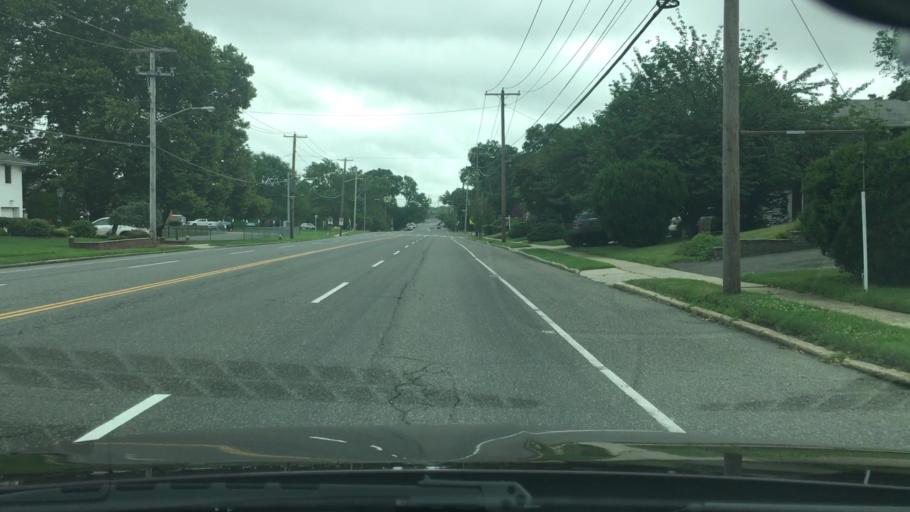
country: US
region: New York
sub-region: Nassau County
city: Jericho
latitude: 40.8017
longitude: -73.5263
